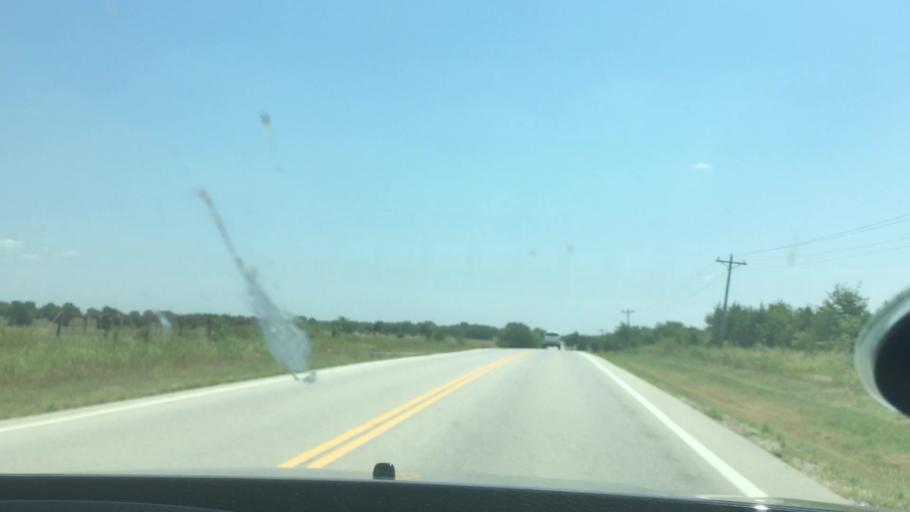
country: US
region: Oklahoma
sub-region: Bryan County
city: Durant
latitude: 34.1541
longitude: -96.3842
